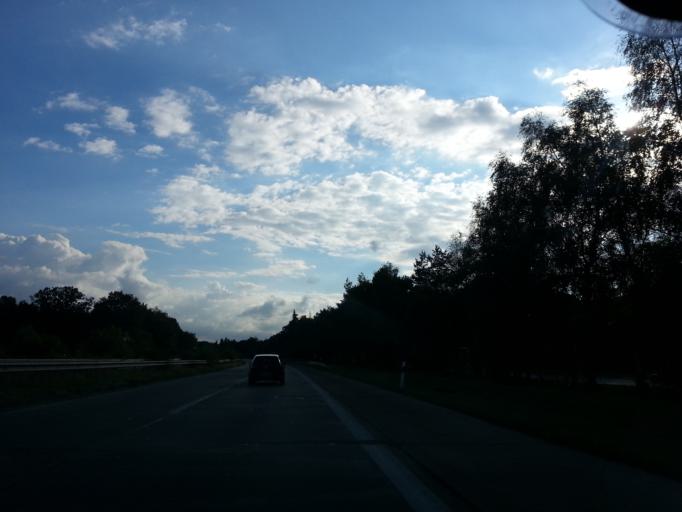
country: DE
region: Schleswig-Holstein
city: Ratekau
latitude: 53.9315
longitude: 10.7306
